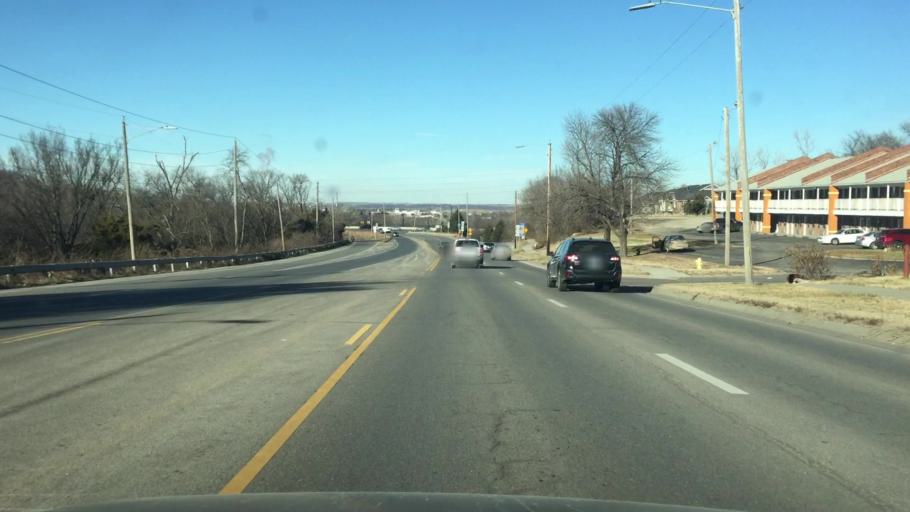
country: US
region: Kansas
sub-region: Douglas County
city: Lawrence
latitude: 38.9697
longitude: -95.2604
